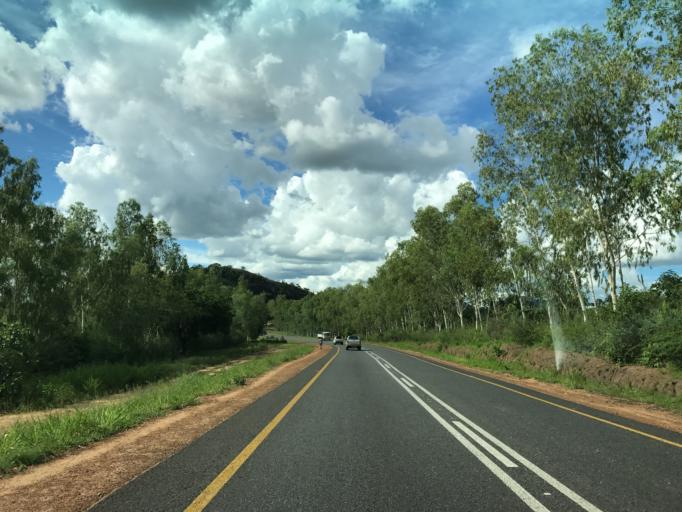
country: MZ
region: Nampula
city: Nampula
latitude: -15.0446
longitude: 39.1378
